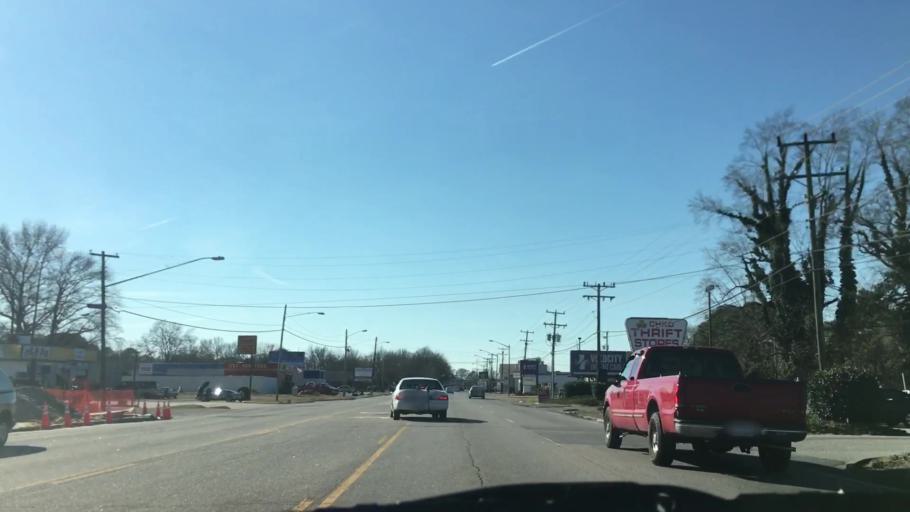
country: US
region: Virginia
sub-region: City of Norfolk
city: Norfolk
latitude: 36.9162
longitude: -76.2345
